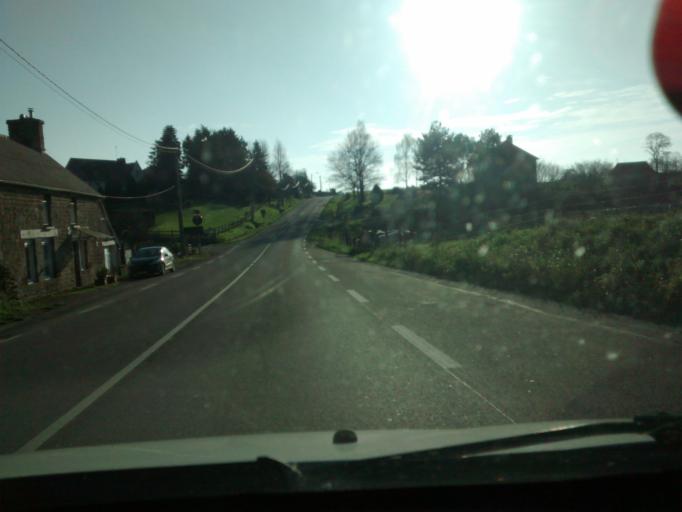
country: FR
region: Brittany
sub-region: Departement d'Ille-et-Vilaine
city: Tremblay
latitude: 48.4201
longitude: -1.4742
